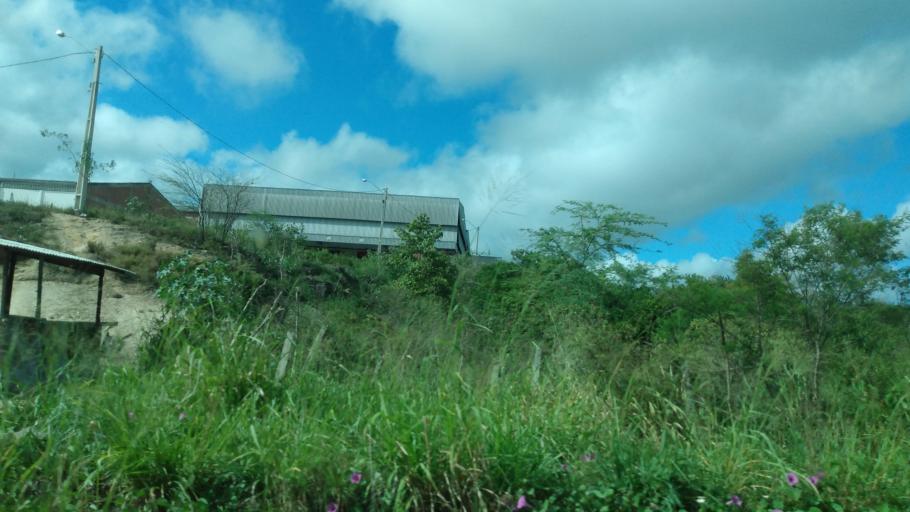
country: BR
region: Pernambuco
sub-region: Caruaru
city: Caruaru
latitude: -8.3054
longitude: -36.0121
